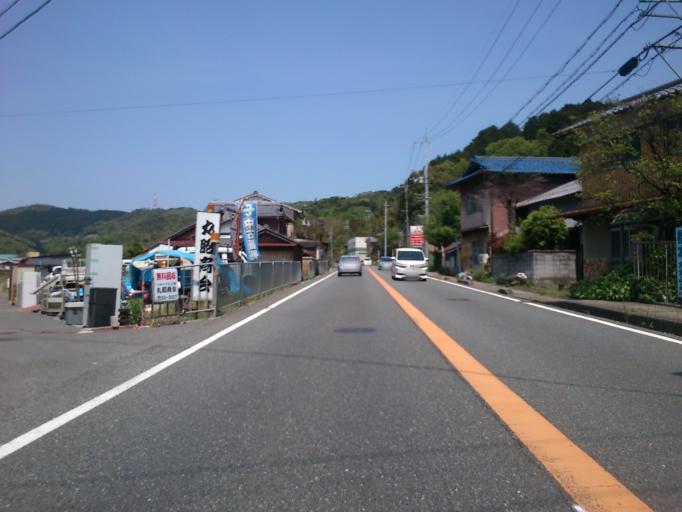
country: JP
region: Kyoto
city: Kameoka
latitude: 35.1130
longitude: 135.4642
